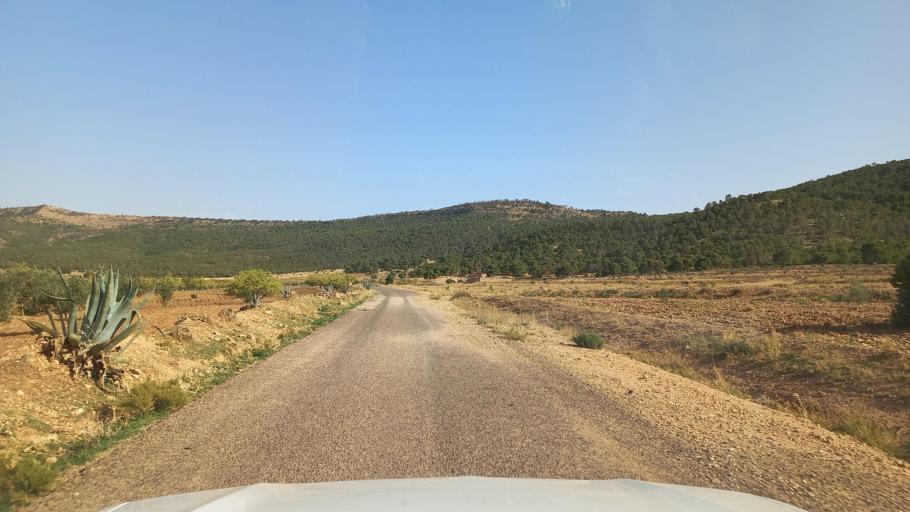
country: TN
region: Al Qasrayn
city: Kasserine
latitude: 35.3373
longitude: 8.8372
